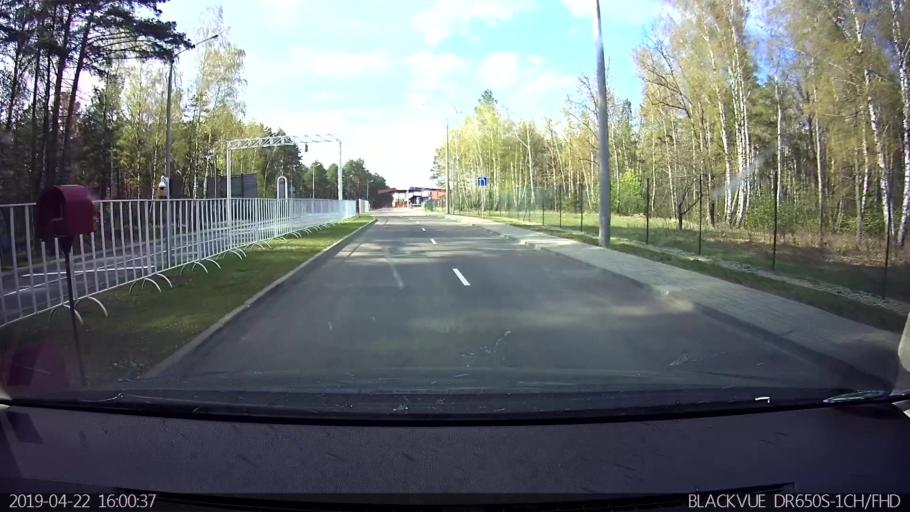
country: PL
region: Podlasie
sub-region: Powiat hajnowski
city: Czeremcha
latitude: 52.4692
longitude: 23.3587
